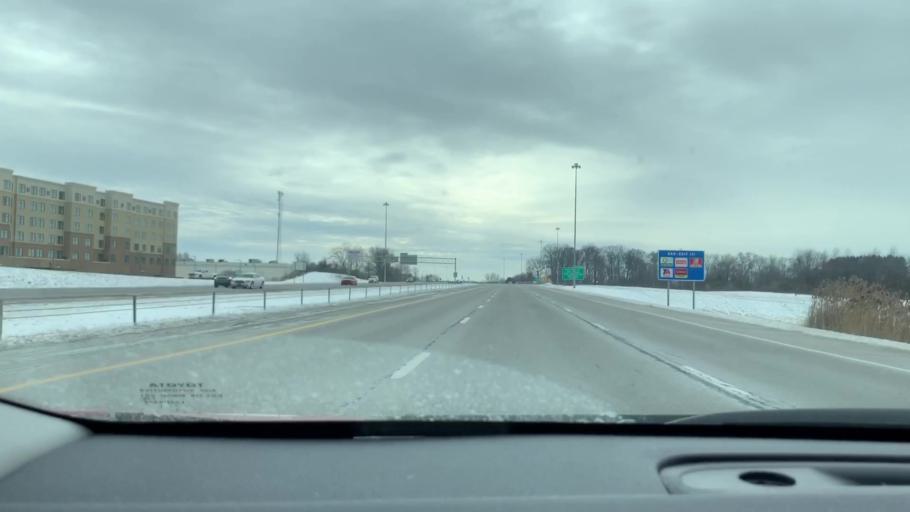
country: US
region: Ohio
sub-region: Stark County
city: North Canton
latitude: 40.8969
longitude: -81.4308
